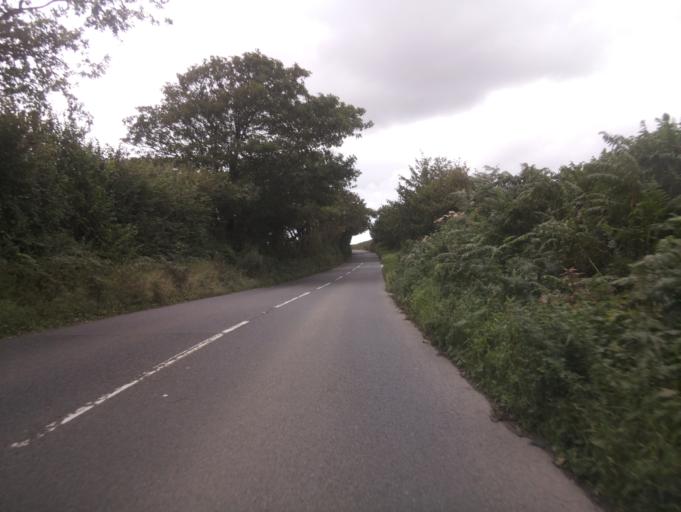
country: GB
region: England
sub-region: Devon
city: Dartmouth
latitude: 50.3532
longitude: -3.6369
